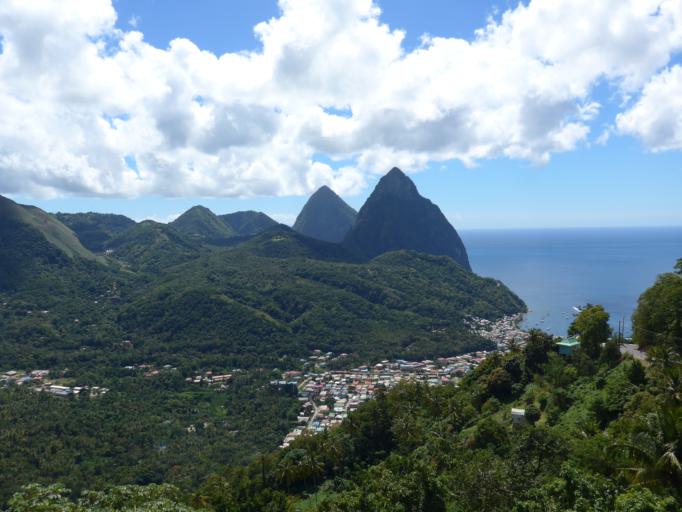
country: LC
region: Soufriere
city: Soufriere
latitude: 13.8671
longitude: -61.0490
